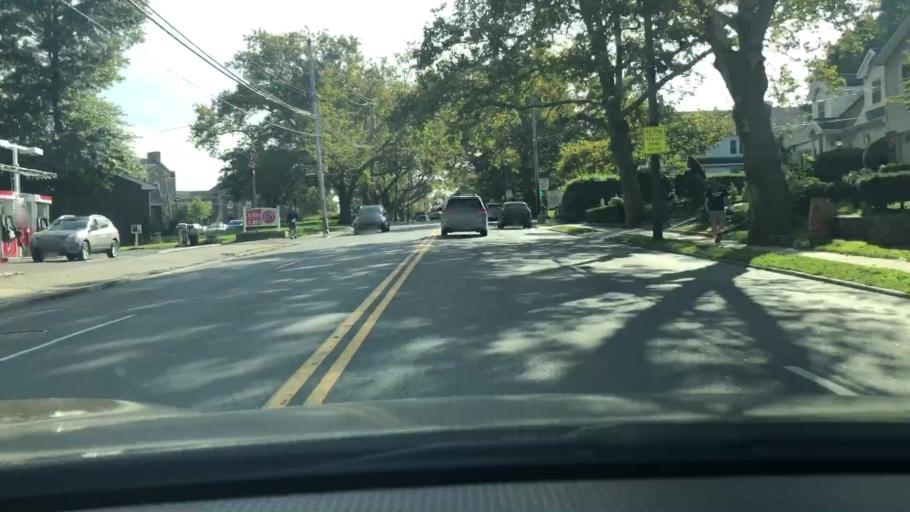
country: US
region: New York
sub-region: Westchester County
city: Tuckahoe
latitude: 40.9631
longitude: -73.8104
